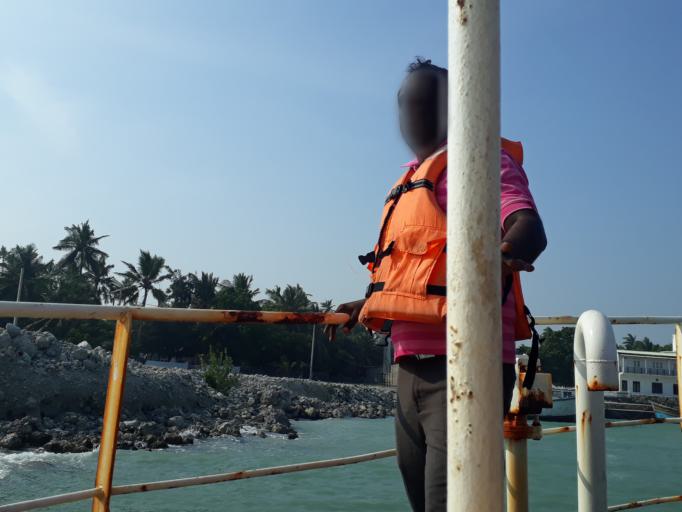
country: LK
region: Northern Province
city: Jaffna
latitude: 9.5289
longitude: 79.7178
